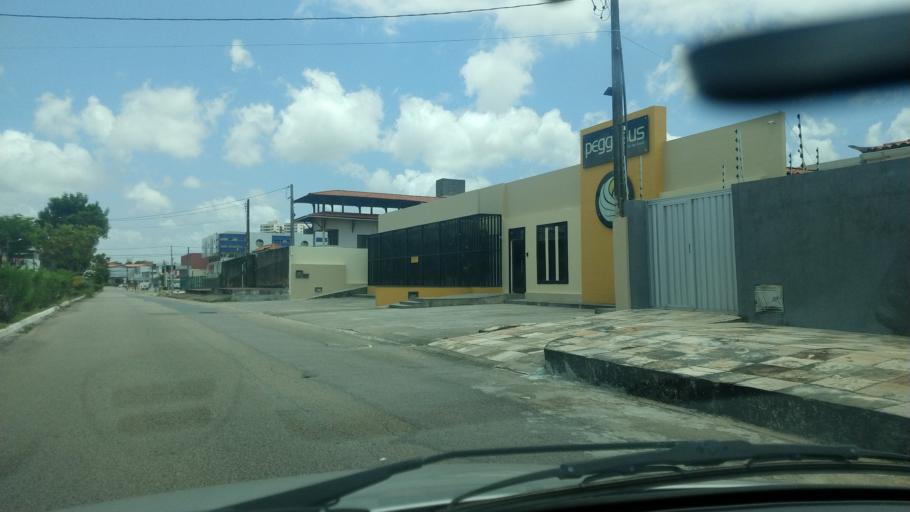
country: BR
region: Rio Grande do Norte
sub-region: Natal
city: Natal
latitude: -5.8491
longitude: -35.2021
